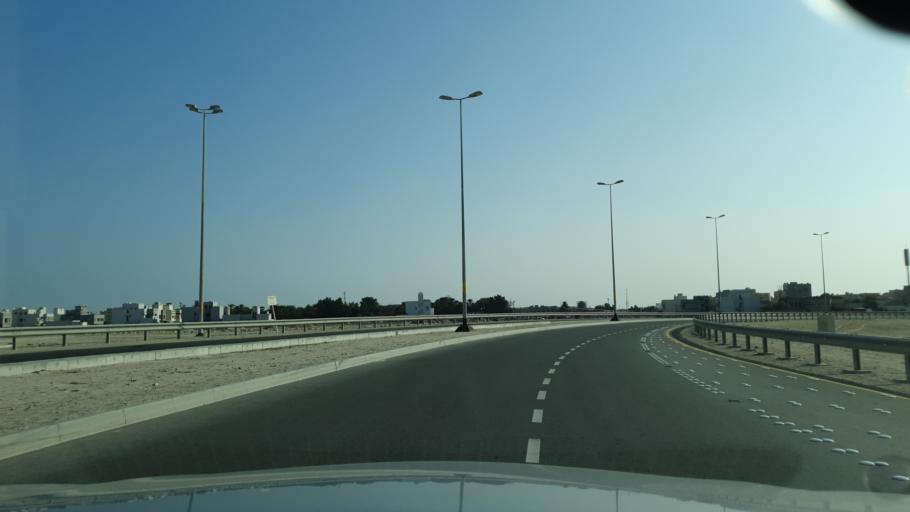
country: BH
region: Manama
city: Jidd Hafs
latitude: 26.2331
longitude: 50.4621
